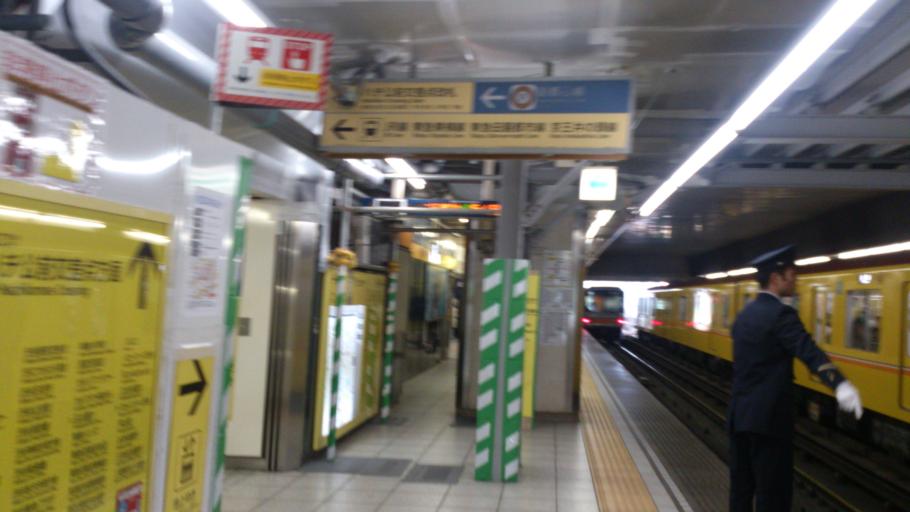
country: JP
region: Tokyo
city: Tokyo
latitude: 35.6589
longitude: 139.7017
